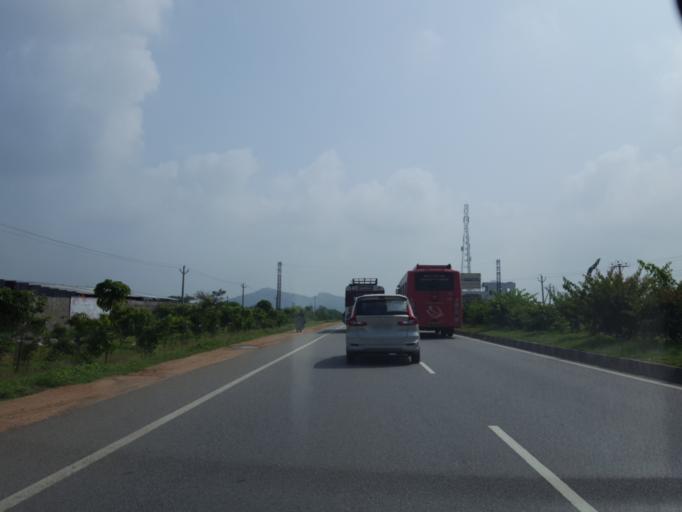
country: IN
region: Telangana
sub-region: Rangareddi
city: Ghatkesar
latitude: 17.2799
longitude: 78.7928
